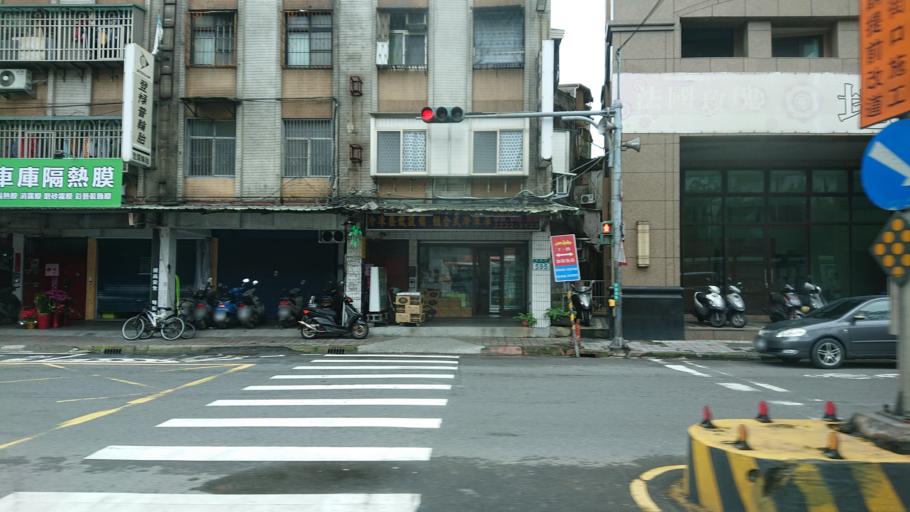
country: TW
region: Taipei
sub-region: Taipei
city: Banqiao
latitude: 24.9938
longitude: 121.4785
